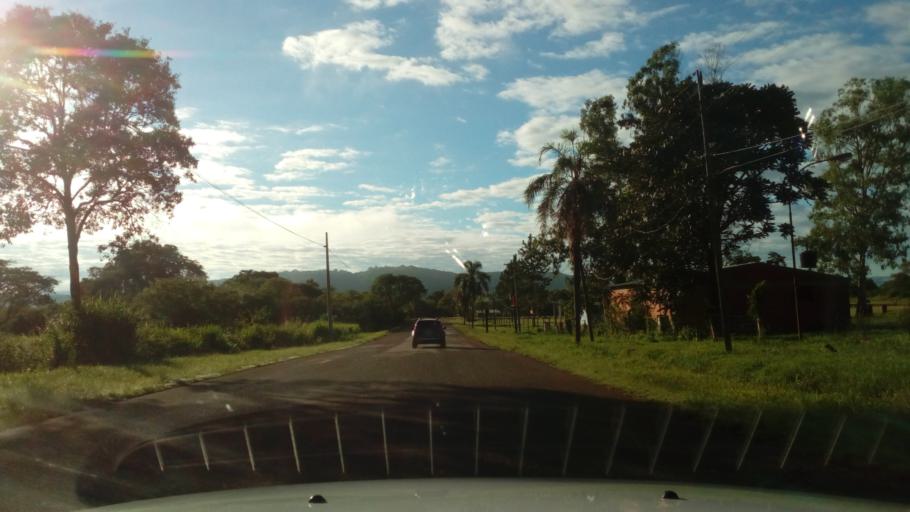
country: AR
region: Misiones
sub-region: Departamento de San Javier
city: San Javier
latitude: -27.8857
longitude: -55.1334
